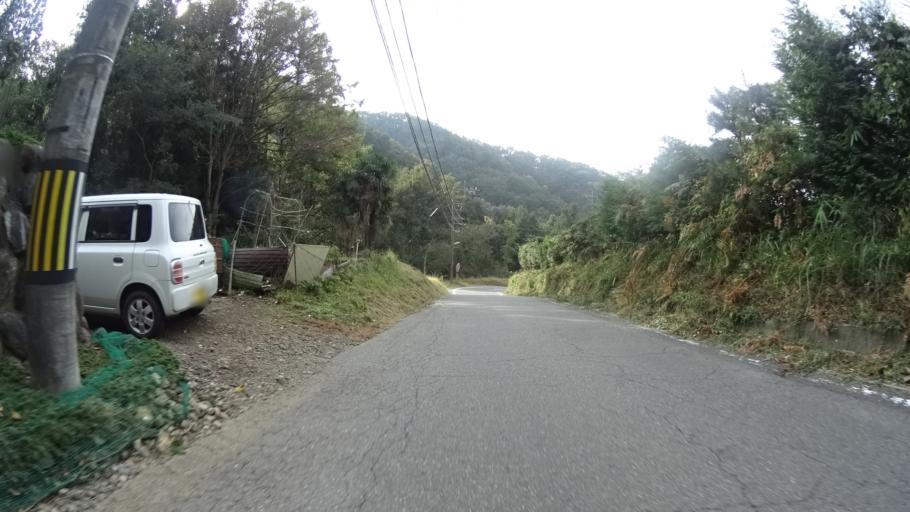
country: JP
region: Yamanashi
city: Otsuki
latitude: 35.6171
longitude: 139.0179
